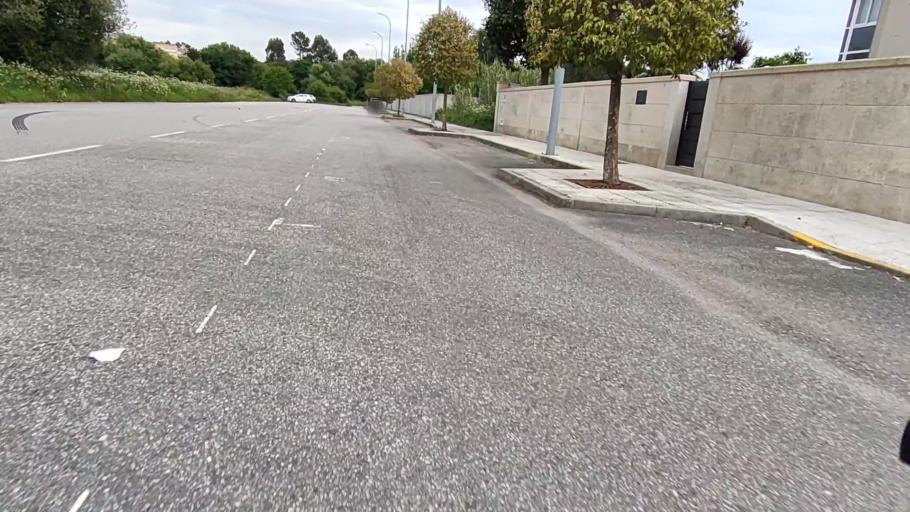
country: ES
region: Galicia
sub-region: Provincia da Coruna
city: Boiro
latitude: 42.6418
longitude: -8.8864
